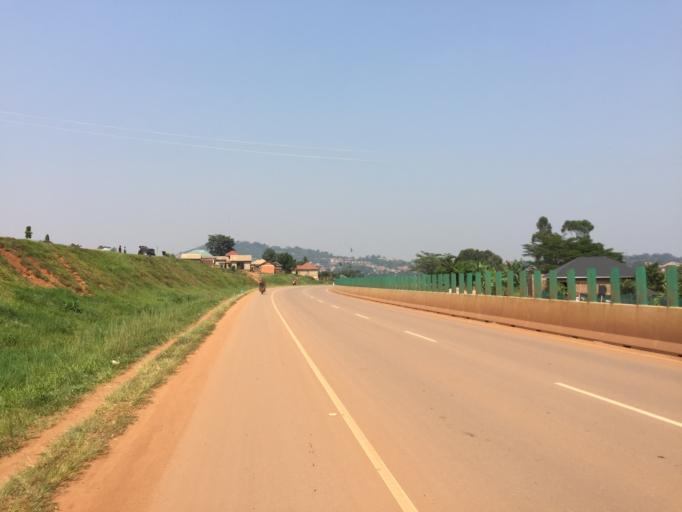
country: UG
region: Central Region
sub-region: Kampala District
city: Kampala
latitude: 0.2335
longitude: 32.6078
